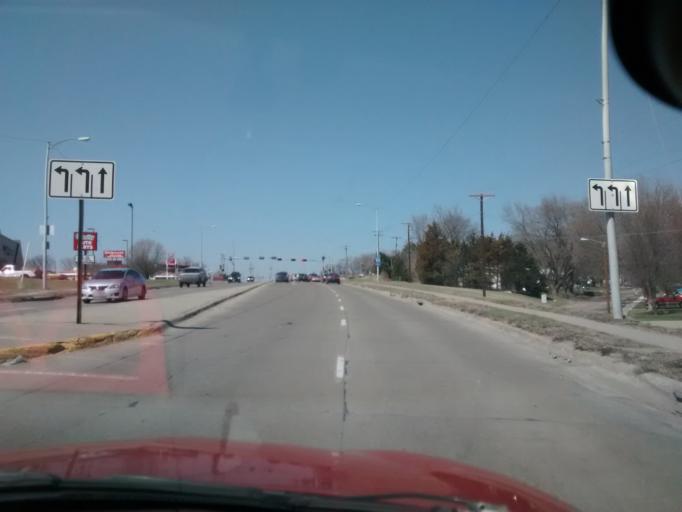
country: US
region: Nebraska
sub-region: Sarpy County
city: Bellevue
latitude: 41.1404
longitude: -95.9084
